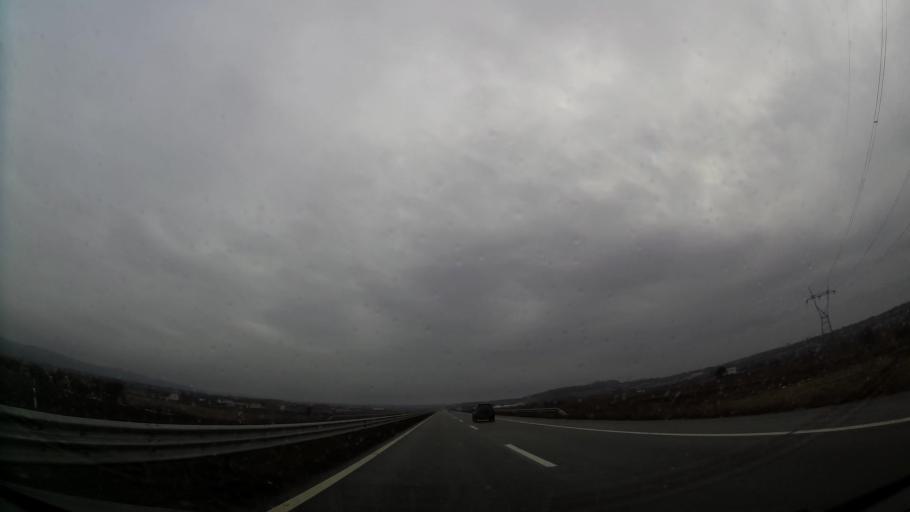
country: XK
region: Ferizaj
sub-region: Komuna e Ferizajt
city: Ferizaj
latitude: 42.4503
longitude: 21.1889
